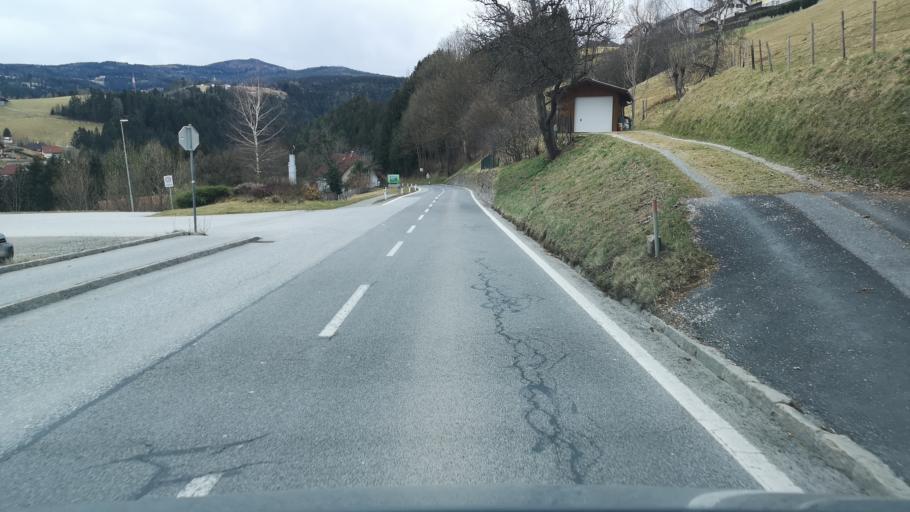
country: AT
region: Styria
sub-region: Politischer Bezirk Weiz
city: Birkfeld
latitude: 47.3517
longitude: 15.6952
